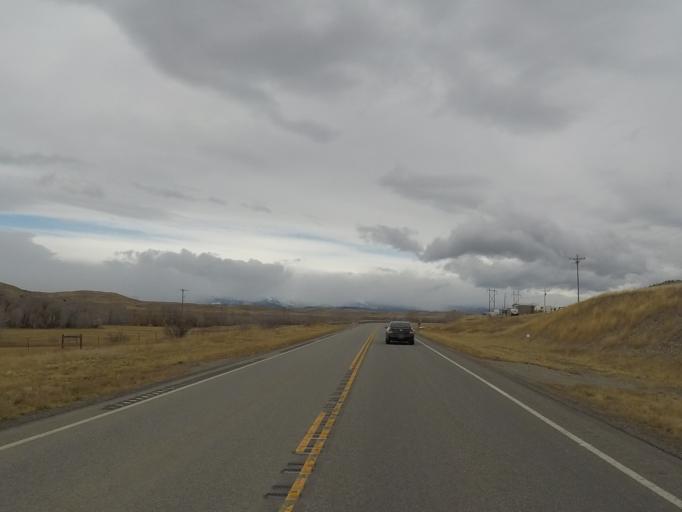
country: US
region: Montana
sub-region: Sweet Grass County
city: Big Timber
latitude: 45.8688
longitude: -109.9427
